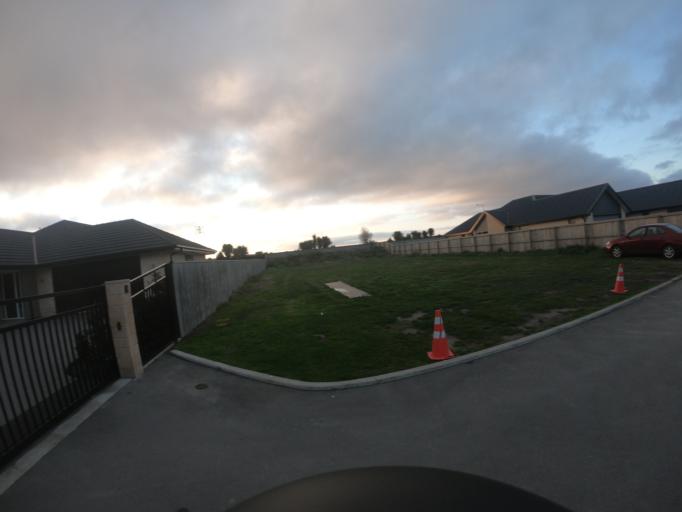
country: NZ
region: Canterbury
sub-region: Selwyn District
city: Prebbleton
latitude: -43.5648
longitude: 172.5554
